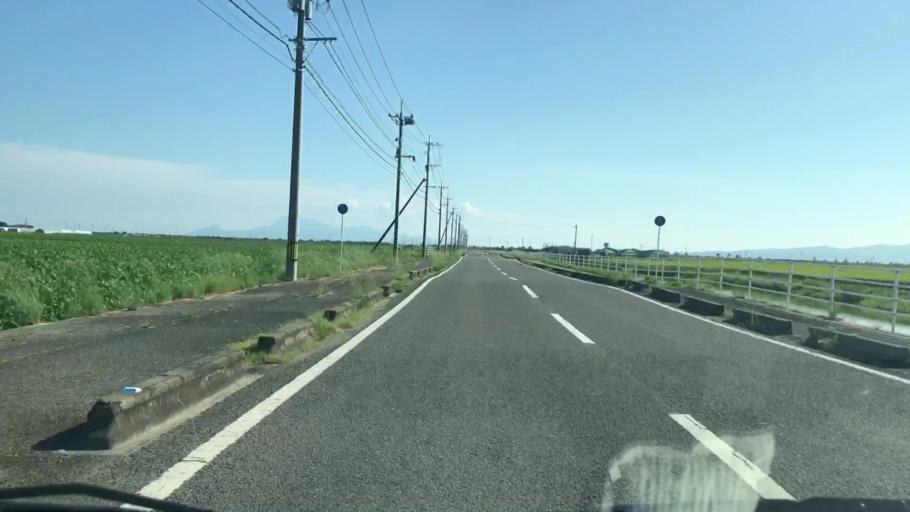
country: JP
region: Saga Prefecture
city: Okawa
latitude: 33.1721
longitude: 130.3108
